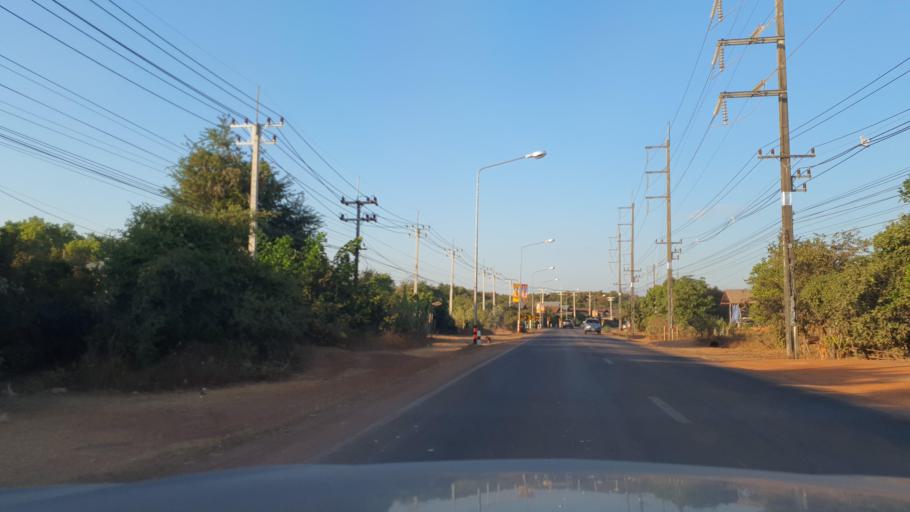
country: TH
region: Nakhon Phanom
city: Si Songkhram
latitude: 17.5840
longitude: 104.2332
